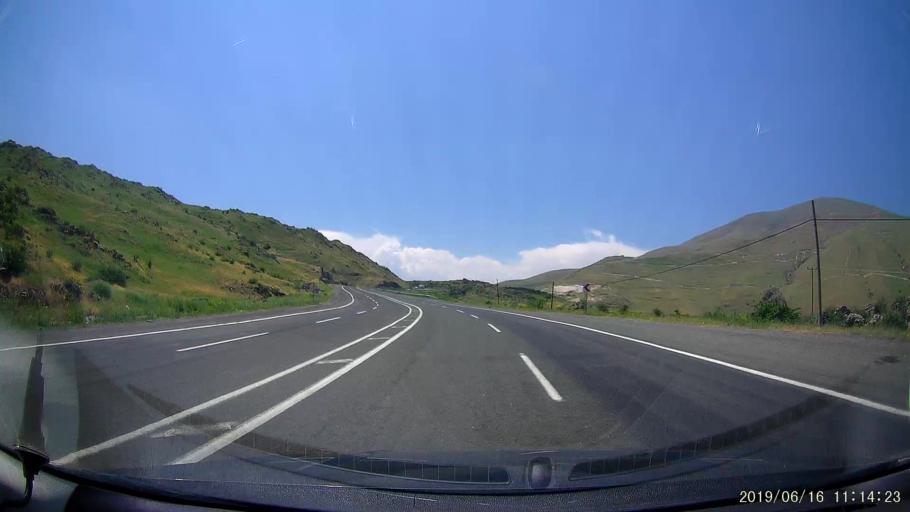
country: TR
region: Igdir
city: Igdir
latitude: 39.7799
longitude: 44.1424
